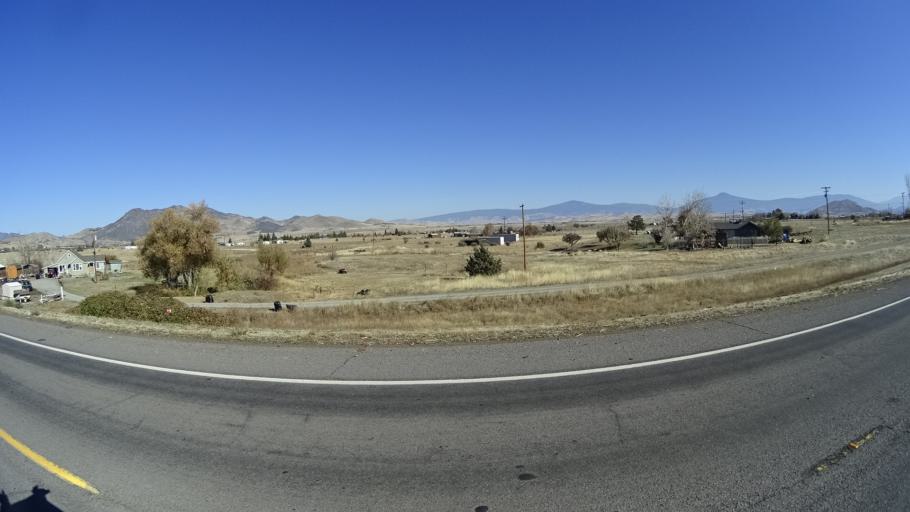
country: US
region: California
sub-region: Siskiyou County
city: Yreka
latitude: 41.7373
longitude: -122.5959
